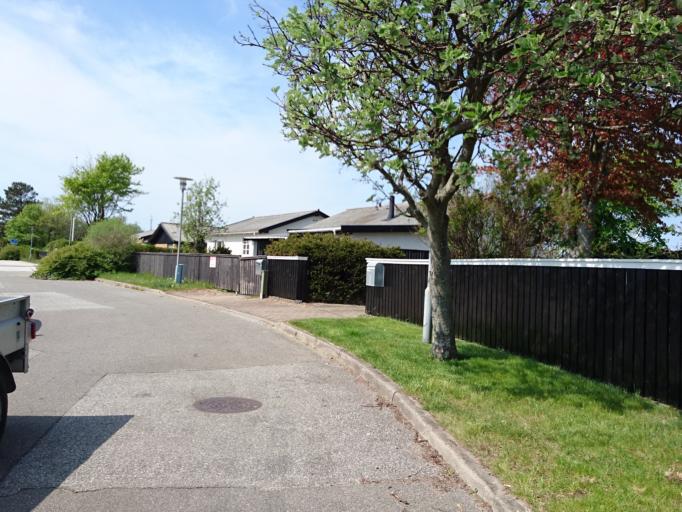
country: DK
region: North Denmark
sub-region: Frederikshavn Kommune
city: Skagen
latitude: 57.7247
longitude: 10.5759
